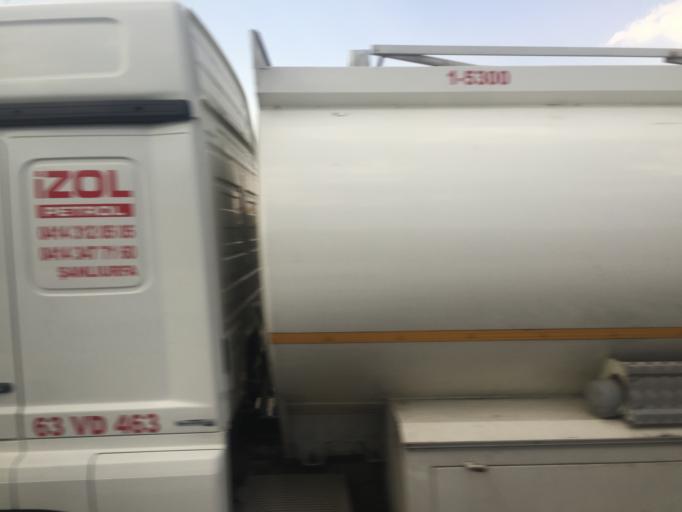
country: TR
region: Sanliurfa
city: Akziyaret
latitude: 37.2658
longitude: 38.7747
